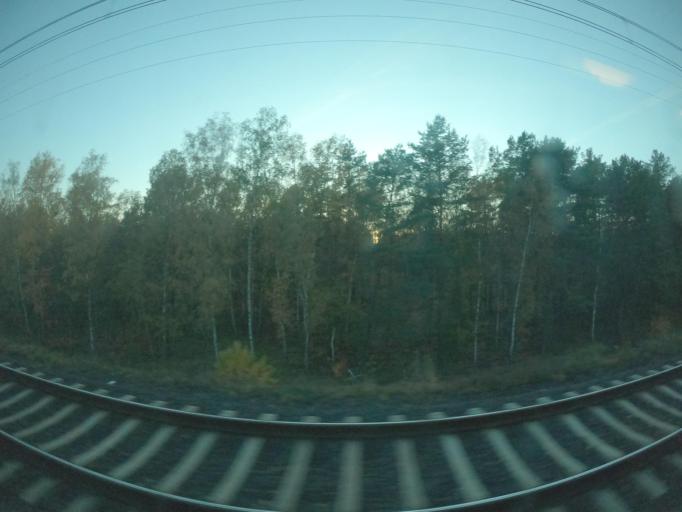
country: PL
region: West Pomeranian Voivodeship
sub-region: Powiat mysliborski
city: Boleszkowice
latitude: 52.7072
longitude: 14.5424
